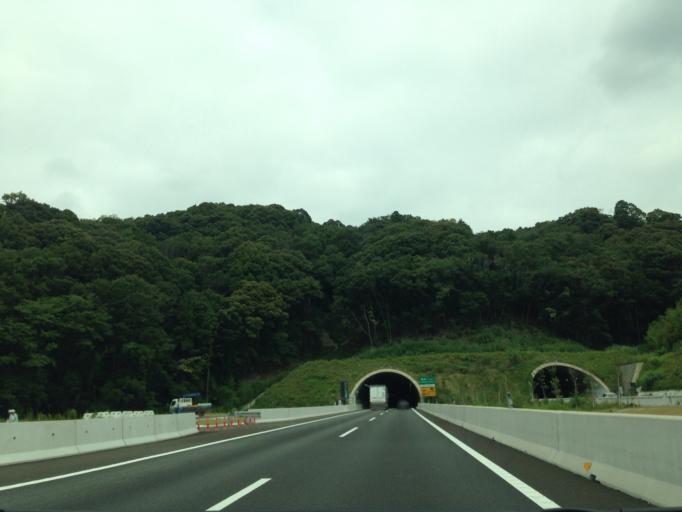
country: JP
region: Aichi
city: Okazaki
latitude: 34.9446
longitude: 137.2573
